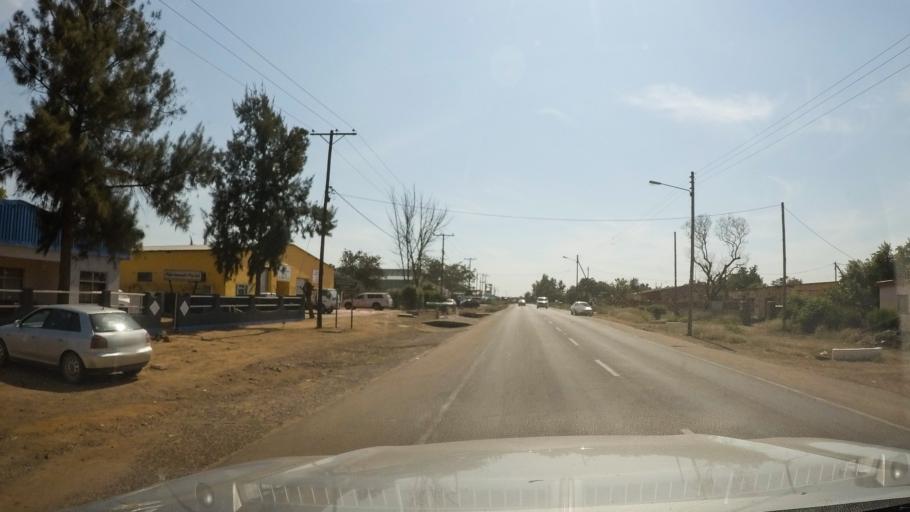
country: BW
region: South East
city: Lobatse
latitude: -25.2044
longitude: 25.6849
